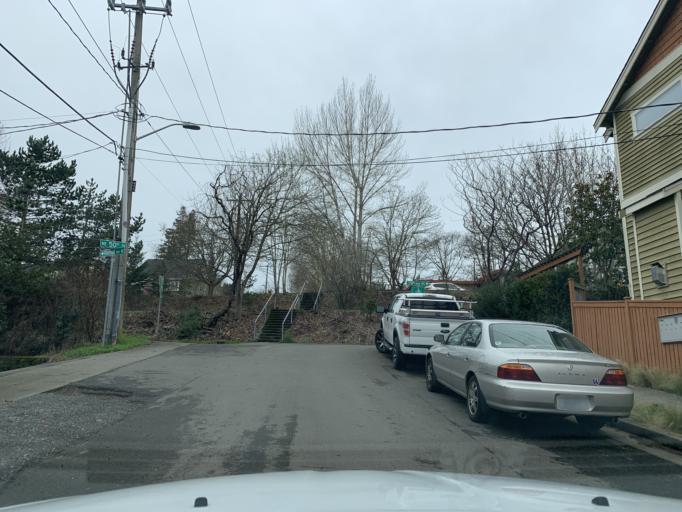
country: US
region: Washington
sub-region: King County
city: Yarrow Point
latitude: 47.6648
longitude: -122.2850
